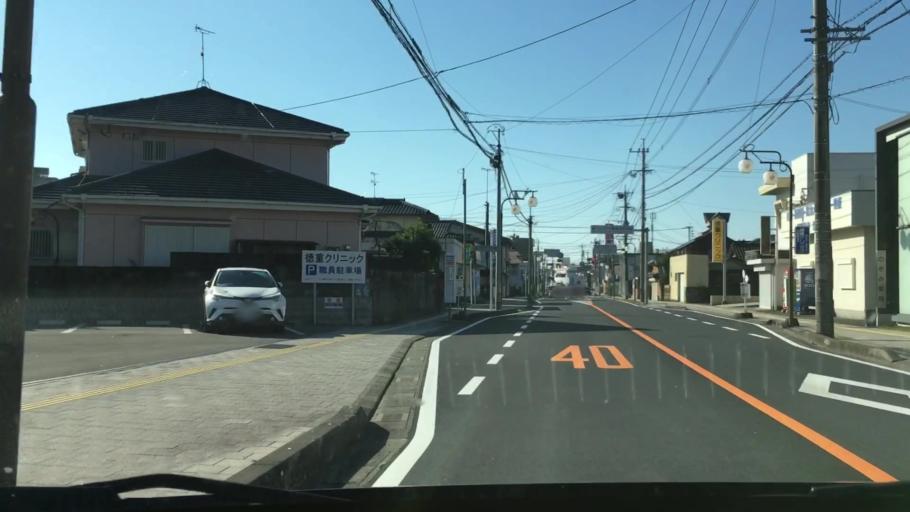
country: JP
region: Kagoshima
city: Kajiki
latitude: 31.7422
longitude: 130.6685
